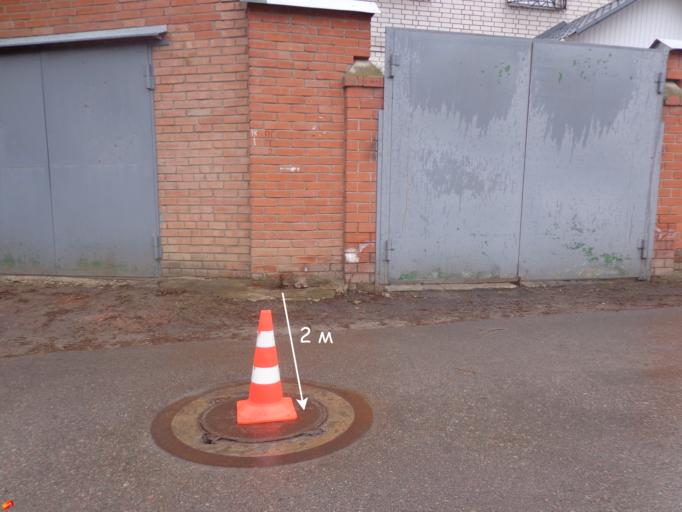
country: RU
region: Voronezj
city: Voronezh
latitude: 51.7177
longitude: 39.2269
